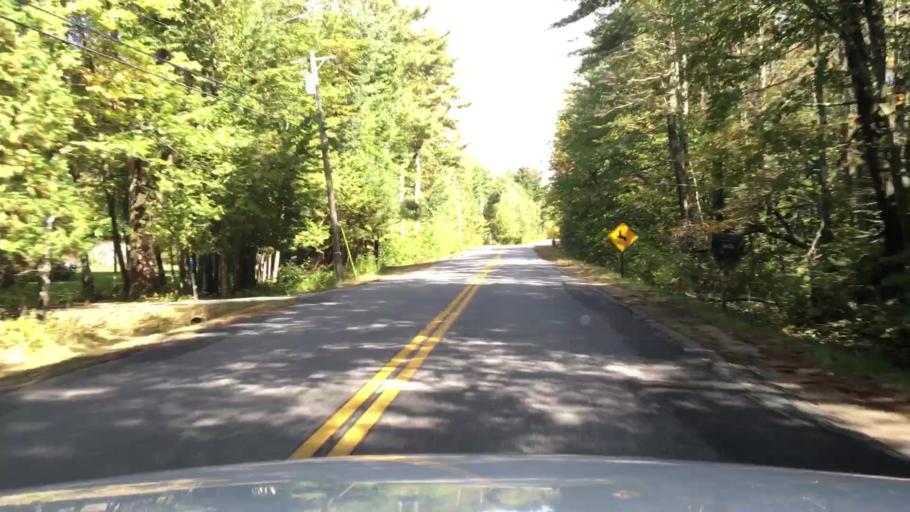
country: US
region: Maine
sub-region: Cumberland County
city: Brunswick
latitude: 43.9460
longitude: -69.8967
